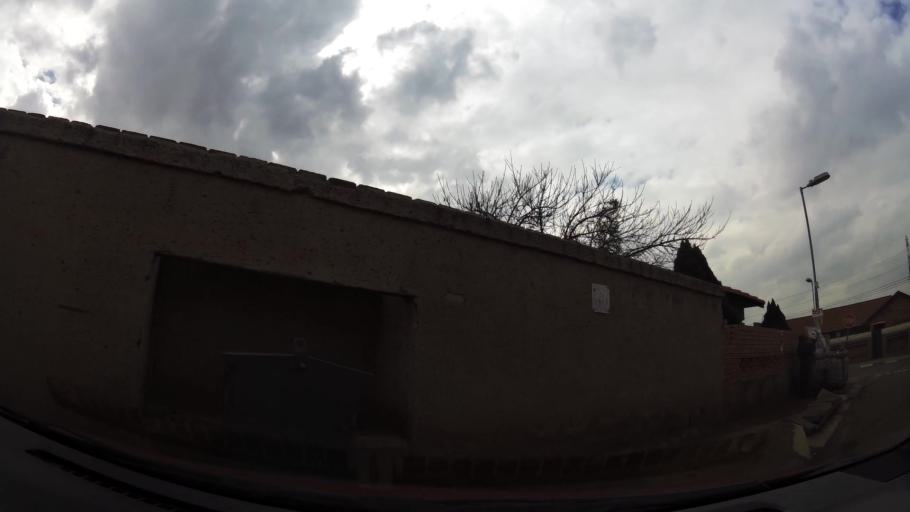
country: ZA
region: Gauteng
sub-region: City of Johannesburg Metropolitan Municipality
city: Soweto
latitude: -26.2505
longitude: 27.8358
